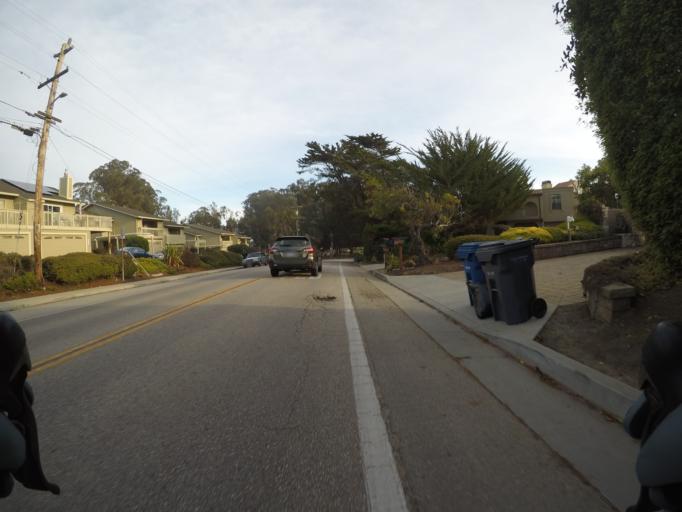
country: US
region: California
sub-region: Santa Cruz County
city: Opal Cliffs
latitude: 36.9575
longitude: -121.9791
